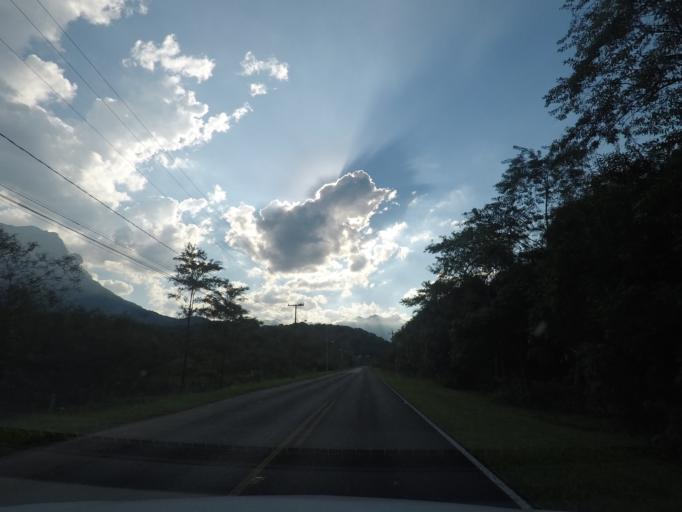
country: BR
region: Parana
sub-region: Antonina
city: Antonina
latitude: -25.4469
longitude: -48.8716
